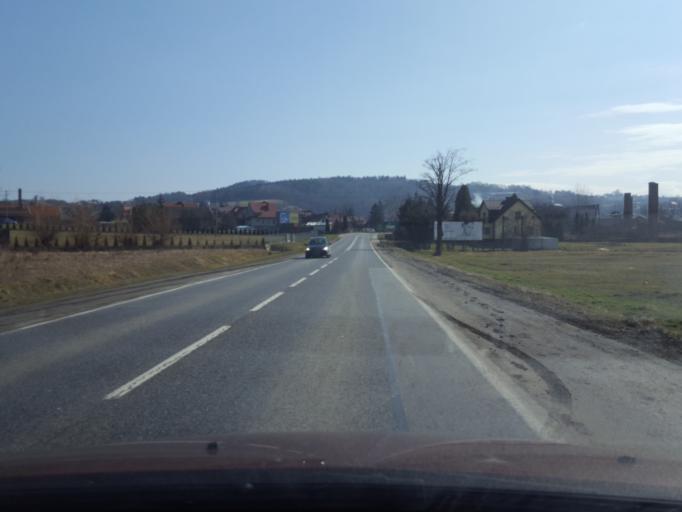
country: PL
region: Lesser Poland Voivodeship
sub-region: Powiat nowosadecki
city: Chelmiec
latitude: 49.6762
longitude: 20.6777
